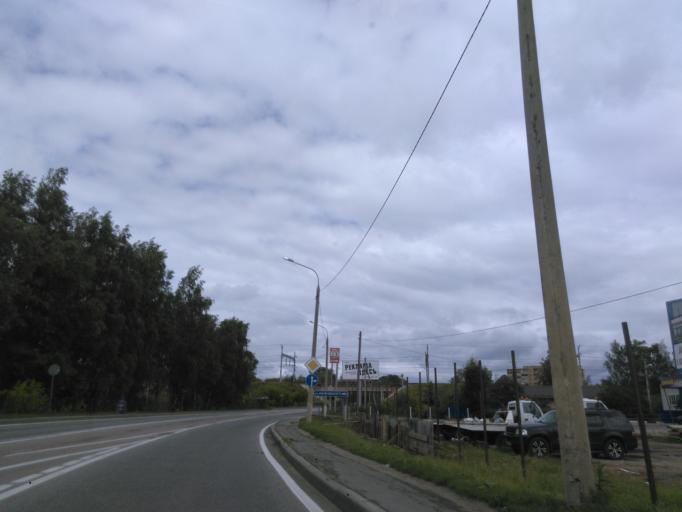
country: RU
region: Moskovskaya
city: Solnechnogorsk
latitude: 56.1869
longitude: 36.9629
